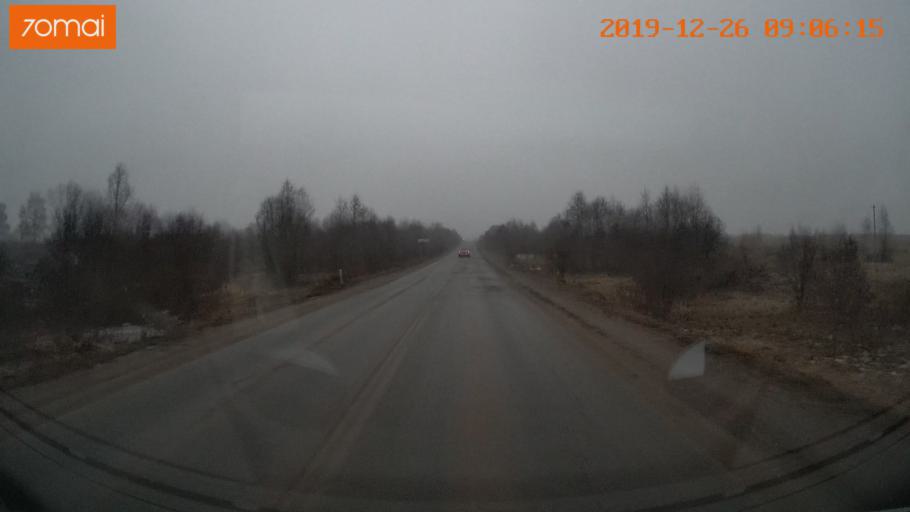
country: RU
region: Vologda
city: Gryazovets
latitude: 58.8341
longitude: 40.2541
